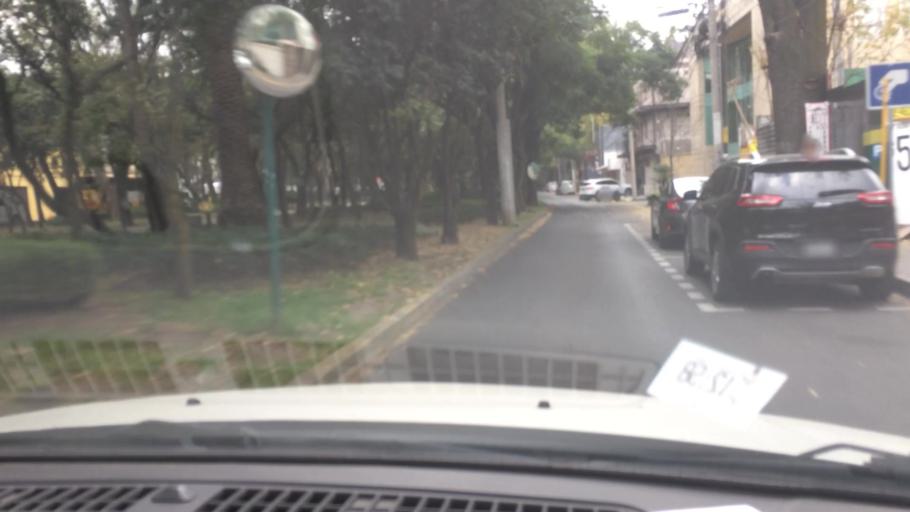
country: MX
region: Mexico City
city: Coyoacan
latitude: 19.3518
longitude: -99.1813
